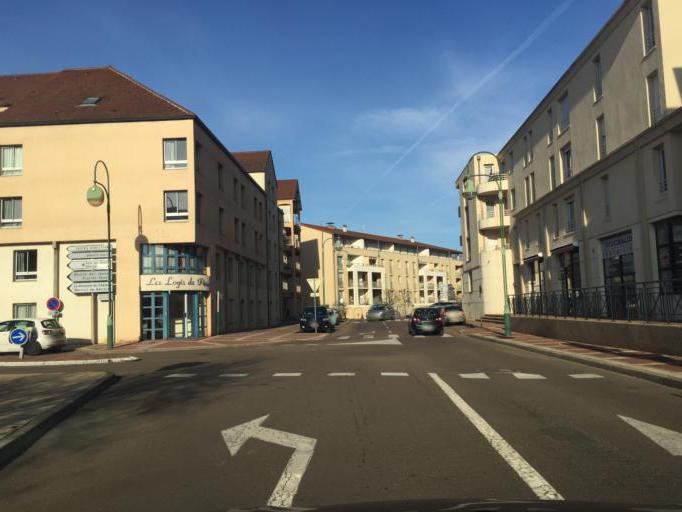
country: FR
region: Bourgogne
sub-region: Departement de Saone-et-Loire
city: Paray-le-Monial
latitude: 46.4519
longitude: 4.1173
